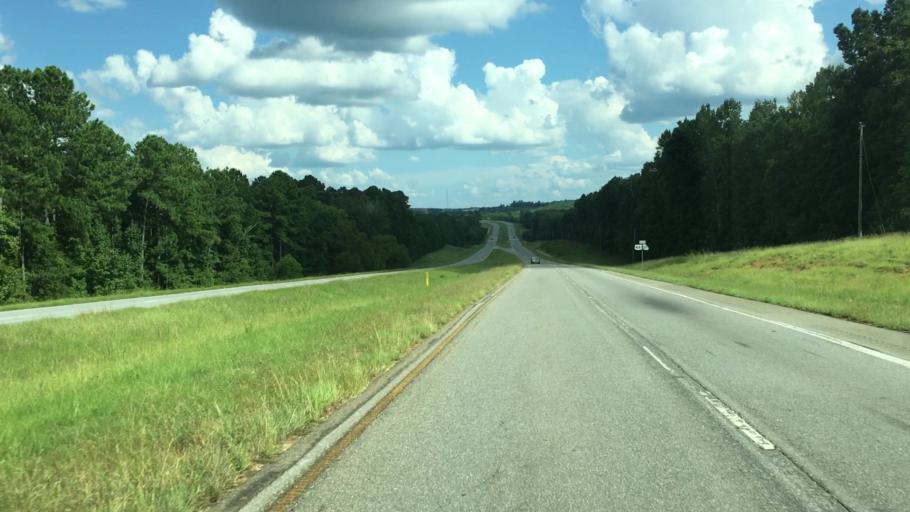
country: US
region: Georgia
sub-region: Wilkinson County
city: Irwinton
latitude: 32.7053
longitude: -83.1291
